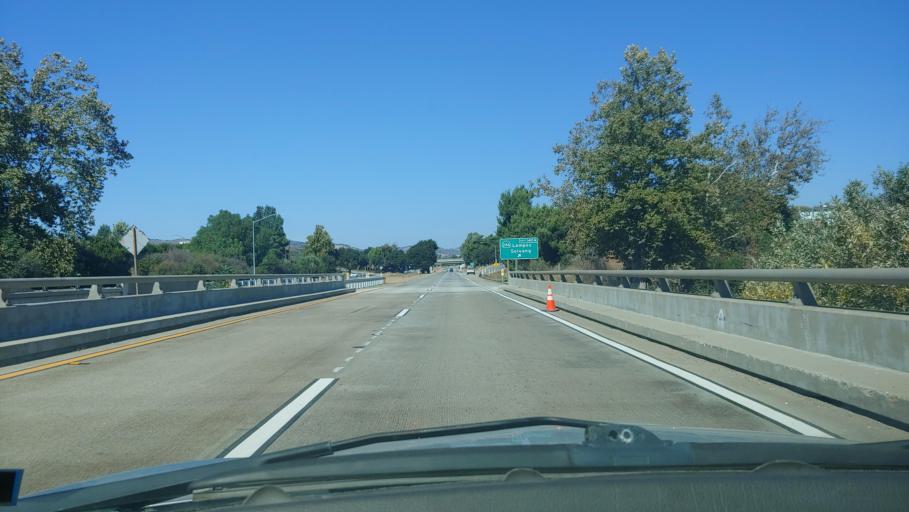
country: US
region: California
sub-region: Santa Barbara County
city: Buellton
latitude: 34.6078
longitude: -120.1908
